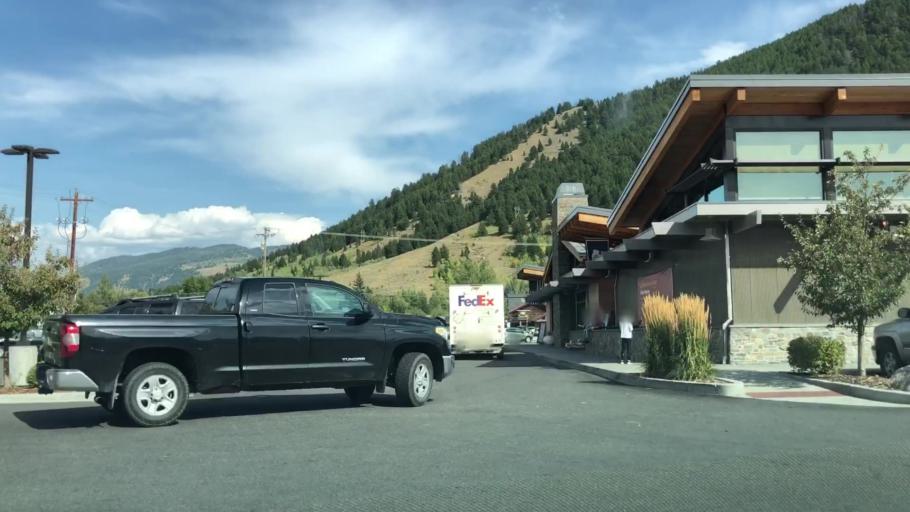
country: US
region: Wyoming
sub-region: Teton County
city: Jackson
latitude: 43.4639
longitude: -110.7949
